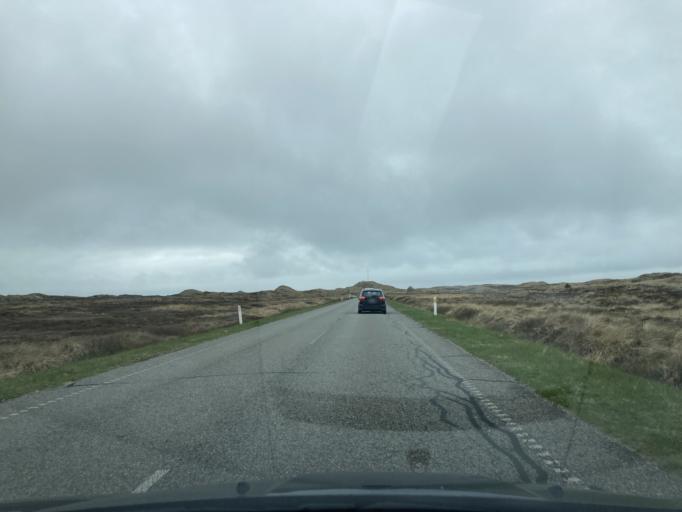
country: DK
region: North Denmark
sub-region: Thisted Kommune
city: Hurup
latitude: 56.9277
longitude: 8.3490
